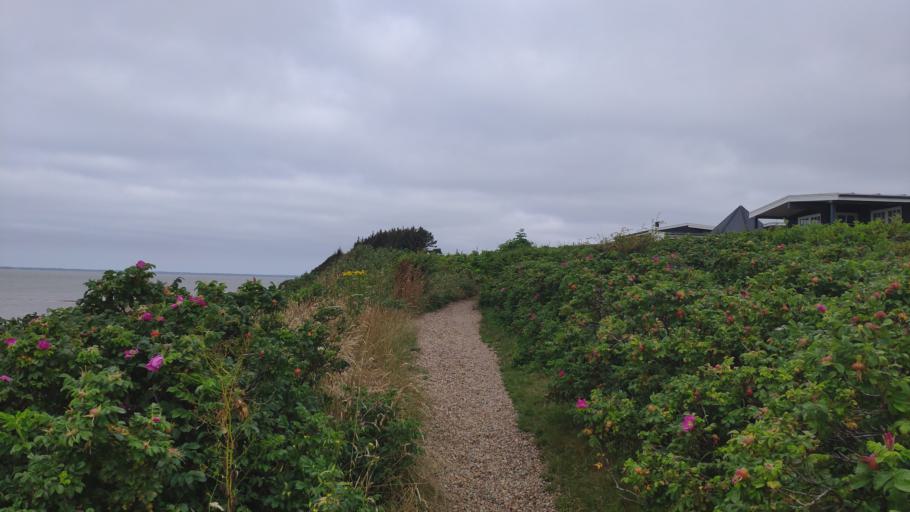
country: DK
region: South Denmark
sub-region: Varde Kommune
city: Oksbol
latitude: 55.5350
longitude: 8.3389
